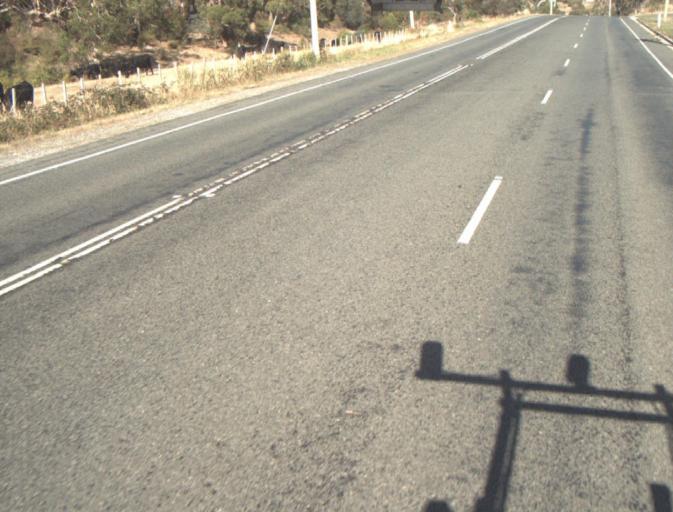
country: AU
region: Tasmania
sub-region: Launceston
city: Mayfield
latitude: -41.3448
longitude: 147.0938
